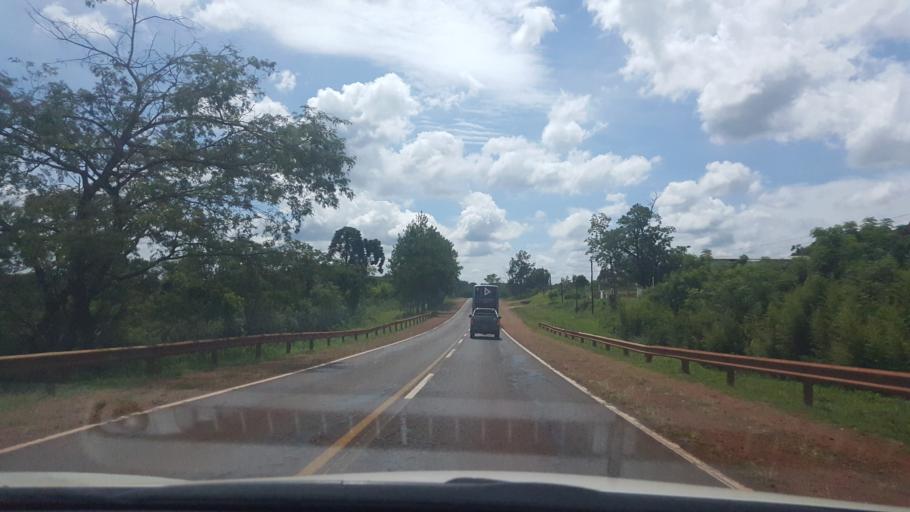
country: AR
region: Misiones
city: Santo Pipo
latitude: -27.1139
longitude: -55.3570
